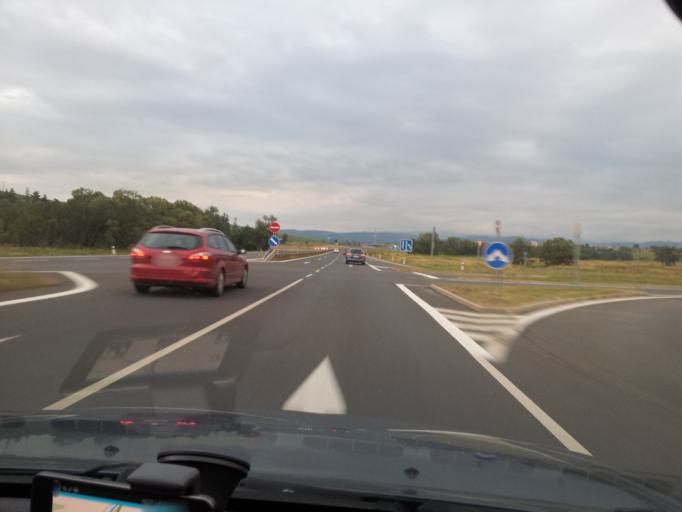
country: SK
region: Presovsky
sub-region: Okres Poprad
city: Poprad
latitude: 49.0944
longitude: 20.3392
